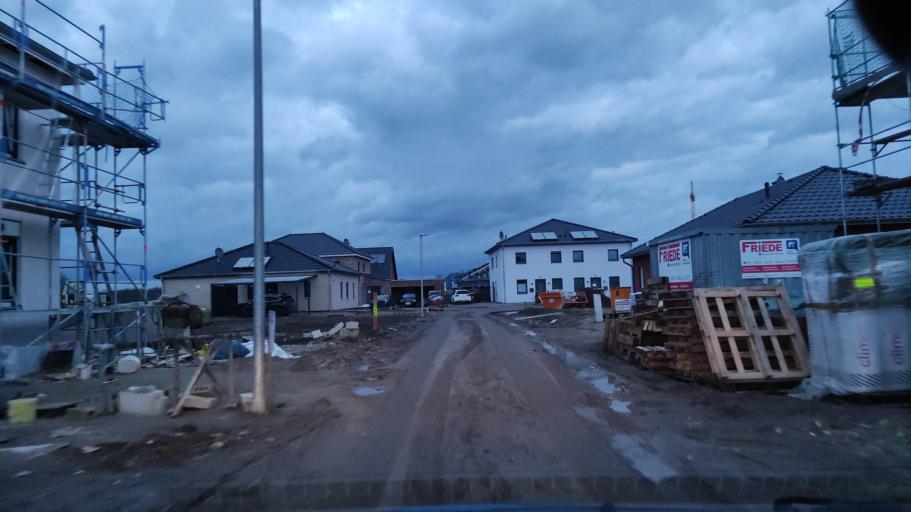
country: DE
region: Lower Saxony
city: Schwarmstedt
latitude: 52.6864
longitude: 9.6200
